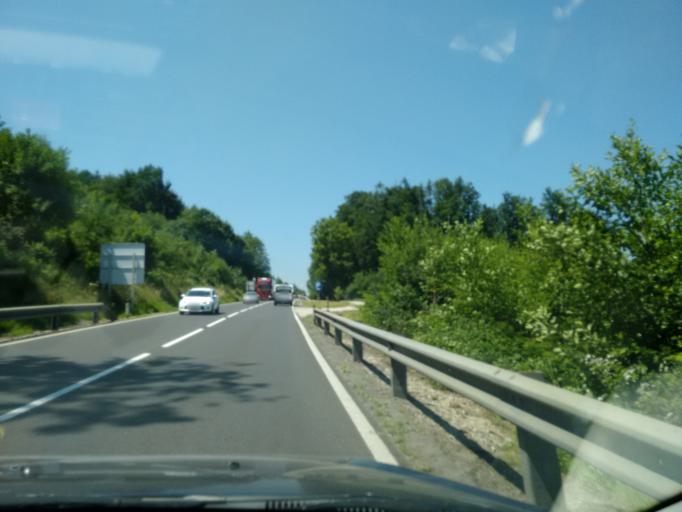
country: AT
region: Upper Austria
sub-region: Politischer Bezirk Gmunden
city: Altmunster
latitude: 47.9516
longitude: 13.7480
